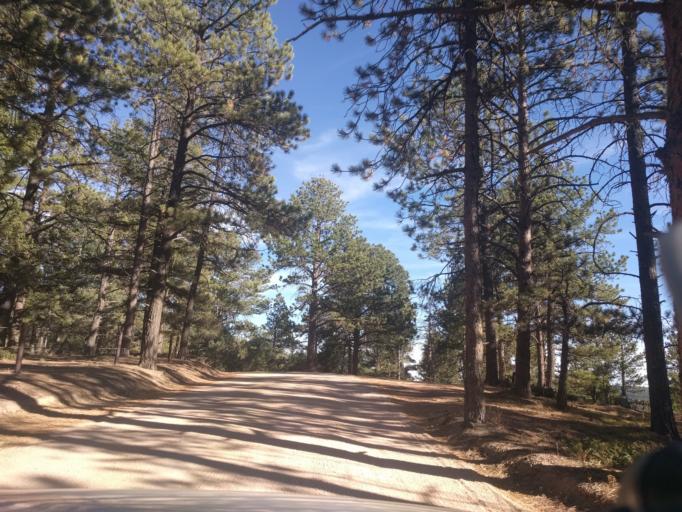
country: US
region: Colorado
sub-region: Douglas County
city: Perry Park
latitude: 39.3034
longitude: -105.0866
